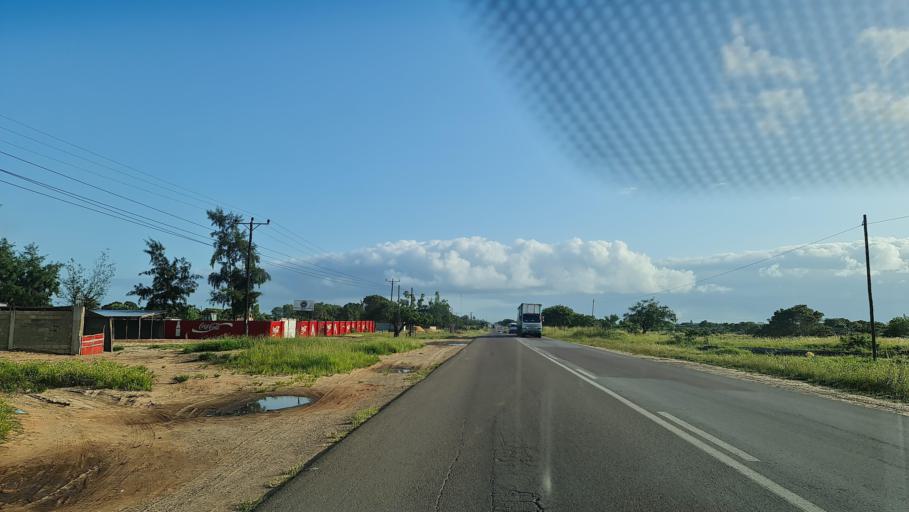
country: MZ
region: Maputo City
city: Maputo
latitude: -25.6806
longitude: 32.6664
